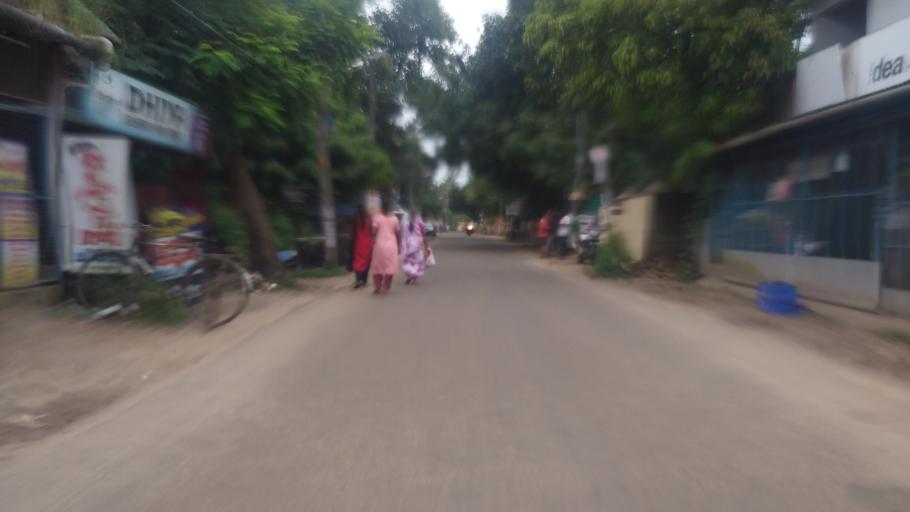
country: IN
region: Kerala
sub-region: Alappuzha
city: Arukutti
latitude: 9.8727
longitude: 76.2898
